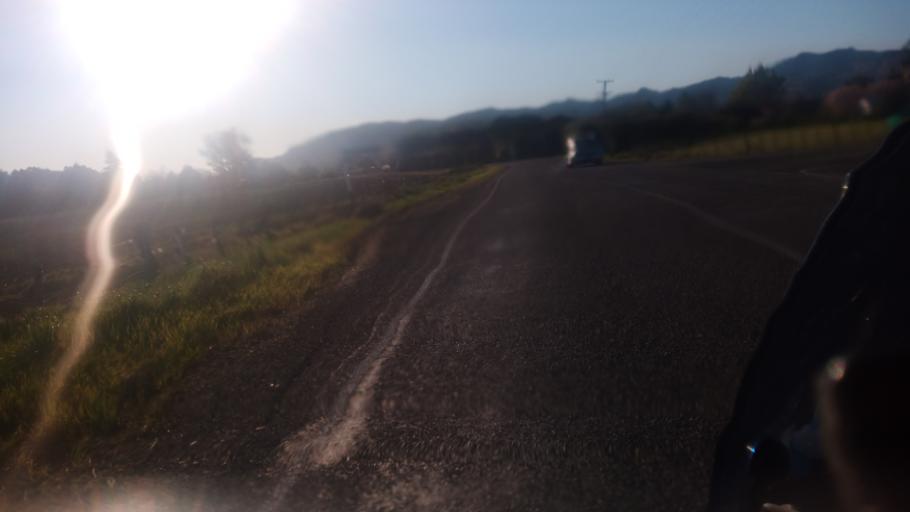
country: NZ
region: Hawke's Bay
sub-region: Wairoa District
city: Wairoa
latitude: -39.0453
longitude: 177.7541
